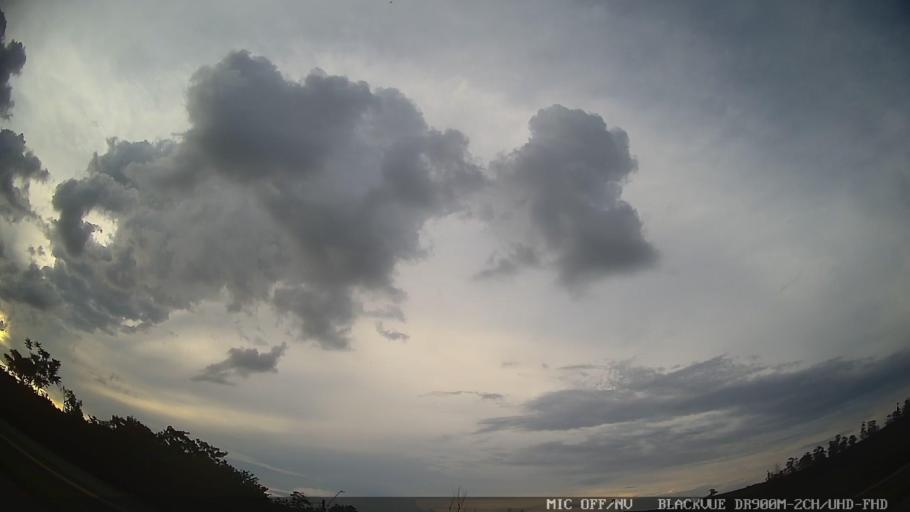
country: BR
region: Sao Paulo
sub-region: Jaguariuna
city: Jaguariuna
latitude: -22.7843
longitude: -47.0282
